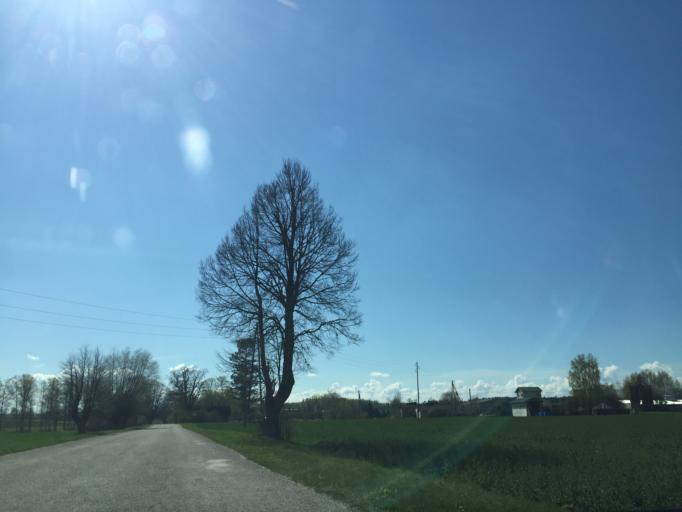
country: LV
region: Strenci
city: Strenci
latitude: 57.5376
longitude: 25.6979
